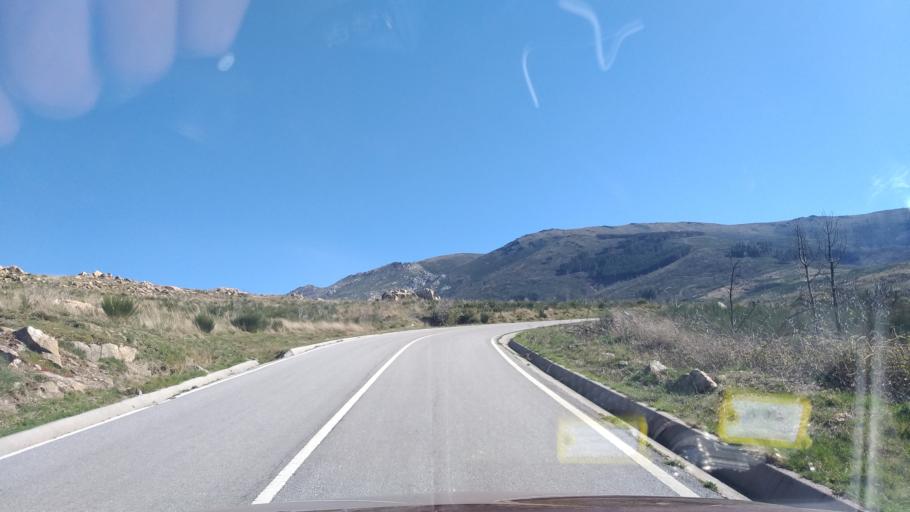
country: PT
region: Guarda
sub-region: Manteigas
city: Manteigas
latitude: 40.4915
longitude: -7.5683
